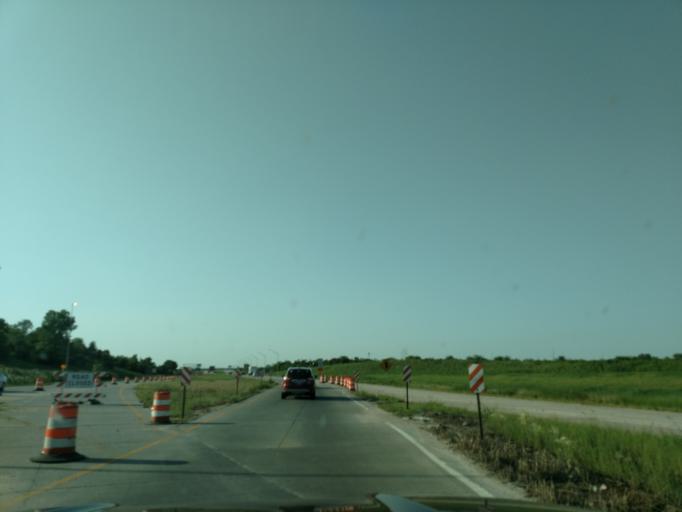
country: US
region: Nebraska
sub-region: Sarpy County
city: Offutt Air Force Base
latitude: 41.1057
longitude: -95.9318
